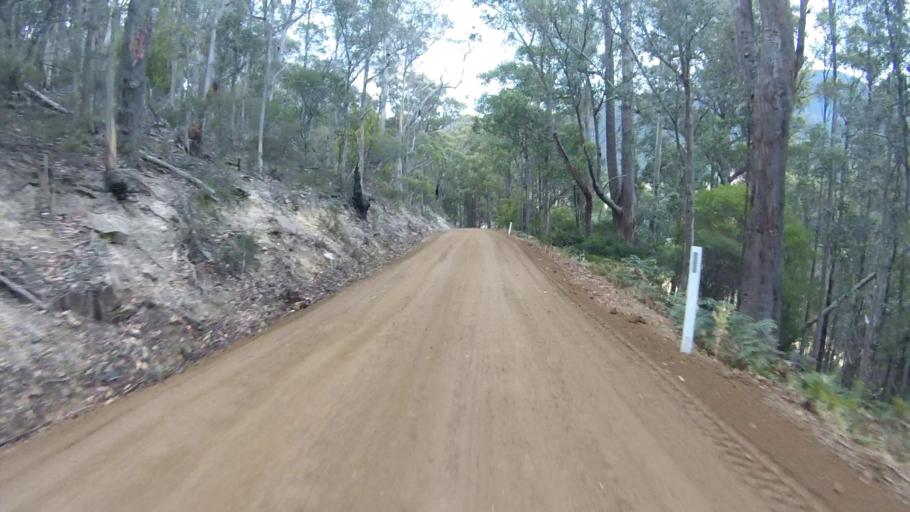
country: AU
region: Tasmania
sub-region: Huon Valley
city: Huonville
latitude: -42.9666
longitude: 147.0467
